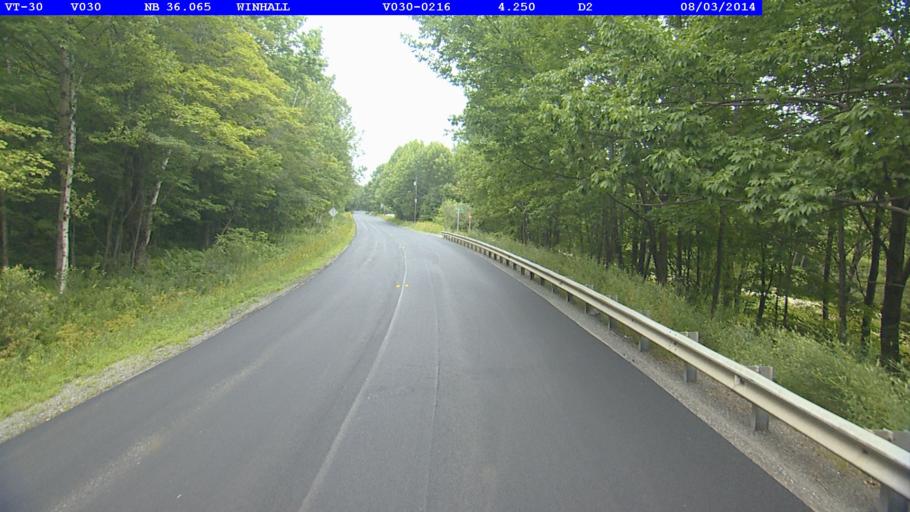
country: US
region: Vermont
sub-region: Bennington County
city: Manchester Center
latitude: 43.1715
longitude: -72.9215
